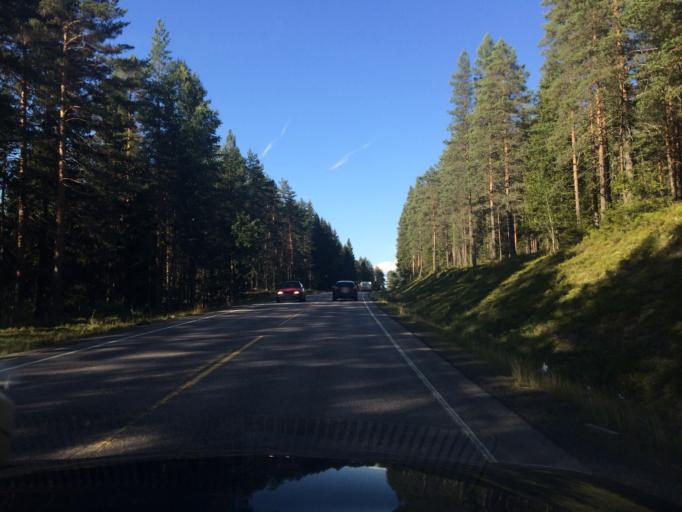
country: NO
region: Hedmark
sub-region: Elverum
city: Elverum
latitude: 60.9646
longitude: 11.7159
